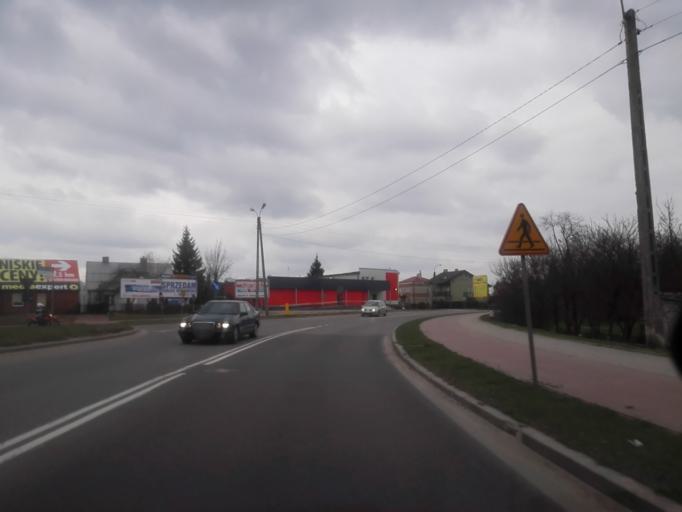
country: PL
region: Podlasie
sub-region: Powiat augustowski
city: Augustow
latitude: 53.8363
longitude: 22.9867
